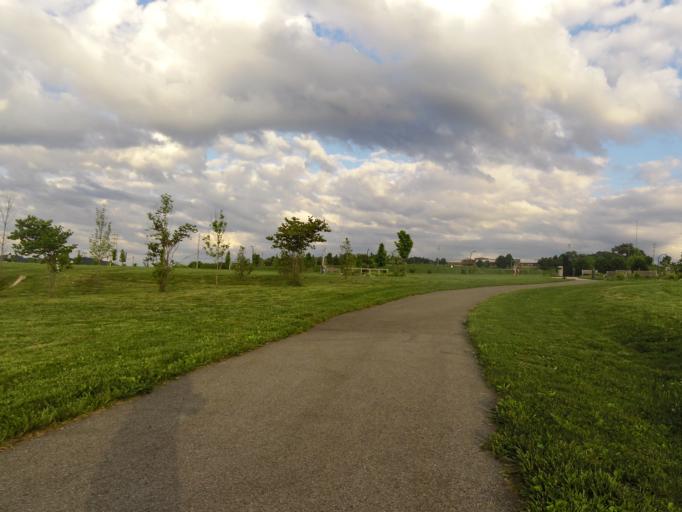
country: US
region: Tennessee
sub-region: Knox County
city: Knoxville
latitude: 35.9462
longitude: -83.9518
